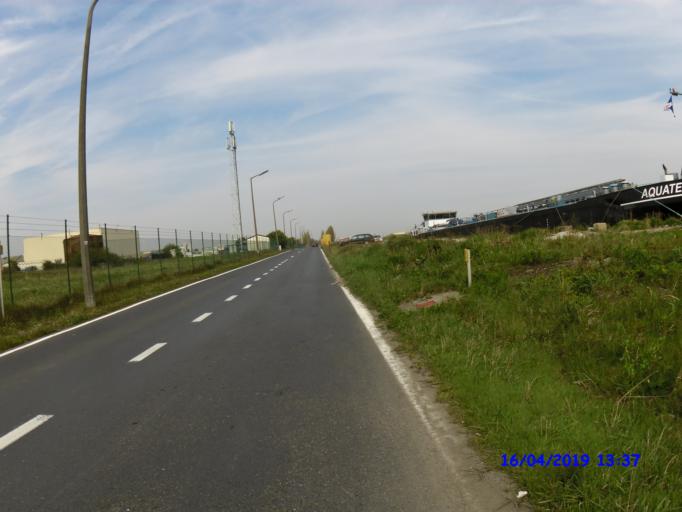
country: BE
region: Flanders
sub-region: Provincie West-Vlaanderen
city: Zeebrugge
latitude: 51.3123
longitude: 3.2012
